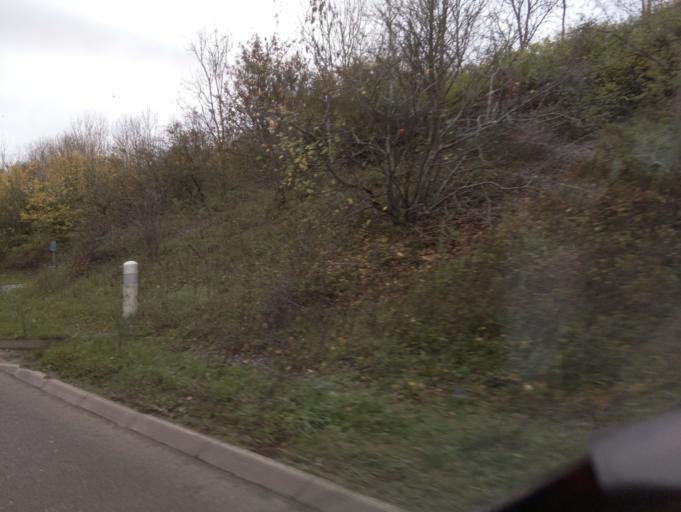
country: GB
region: England
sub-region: Somerset
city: Creech Saint Michael
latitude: 50.9634
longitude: -2.9930
